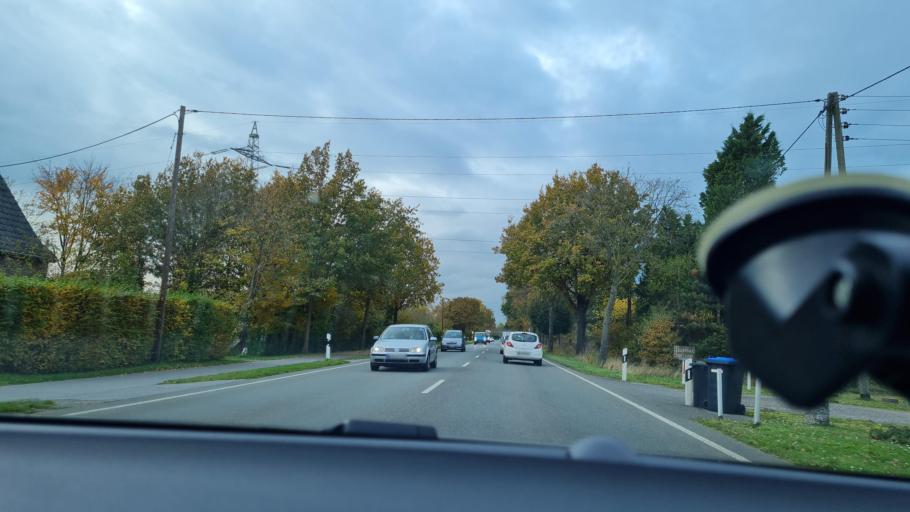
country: DE
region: North Rhine-Westphalia
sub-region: Regierungsbezirk Dusseldorf
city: Voerde
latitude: 51.6168
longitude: 6.6865
